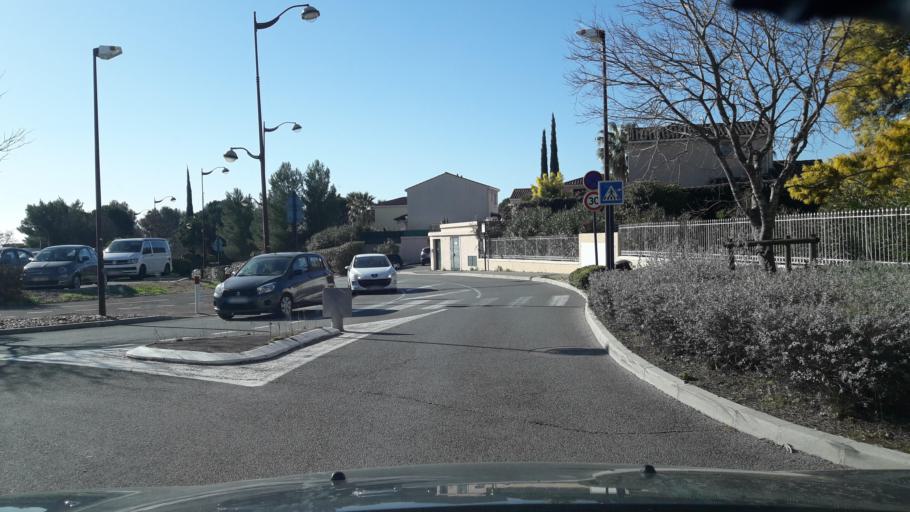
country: FR
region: Provence-Alpes-Cote d'Azur
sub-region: Departement du Var
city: Frejus
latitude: 43.4395
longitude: 6.7488
